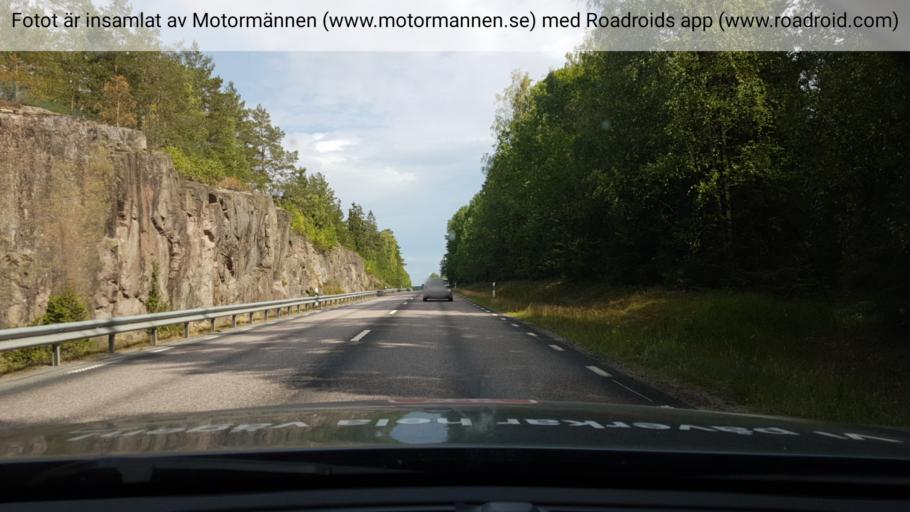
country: SE
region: Uppsala
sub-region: Enkopings Kommun
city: Orsundsbro
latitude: 59.8679
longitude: 17.3234
